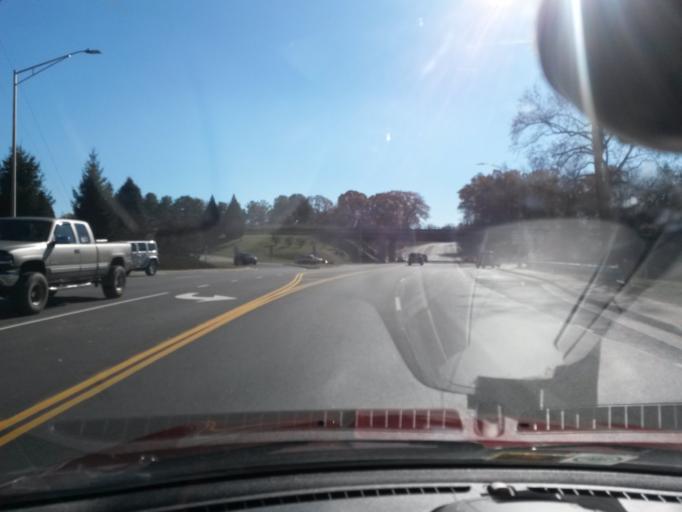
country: US
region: Virginia
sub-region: City of Bedford
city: Bedford
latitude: 37.3260
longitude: -79.5036
